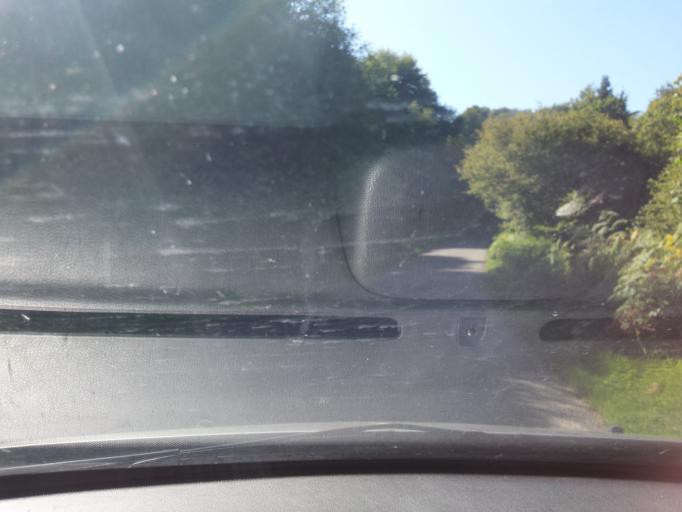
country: FR
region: Brittany
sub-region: Departement des Cotes-d'Armor
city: Plounevez-Quintin
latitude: 48.3369
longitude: -3.2646
